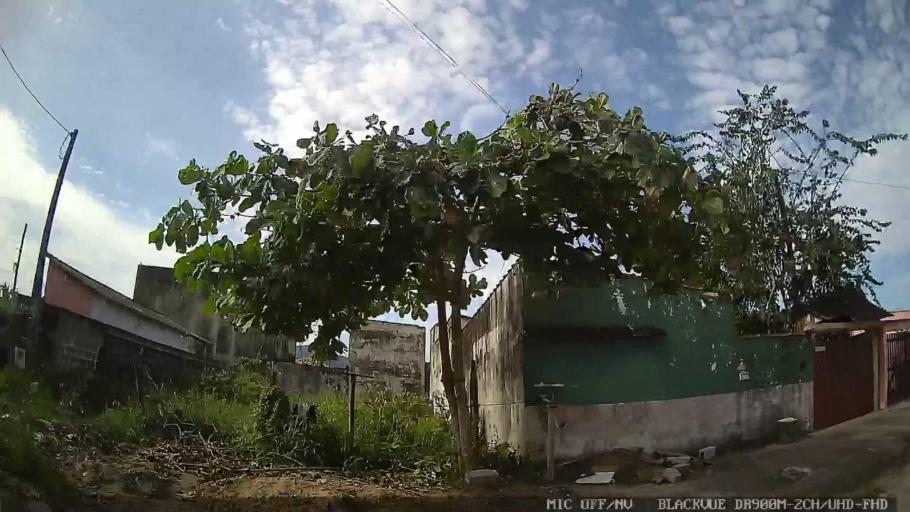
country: BR
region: Sao Paulo
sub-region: Itanhaem
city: Itanhaem
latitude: -24.1588
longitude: -46.7708
